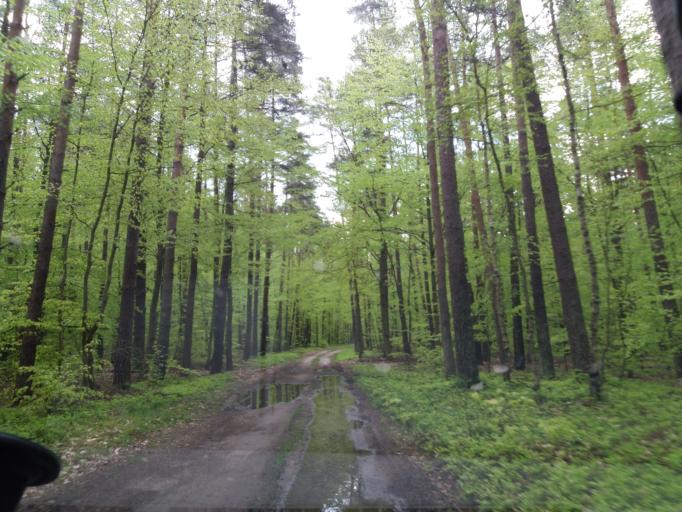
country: PL
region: West Pomeranian Voivodeship
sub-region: Powiat choszczenski
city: Drawno
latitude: 53.1090
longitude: 15.8808
